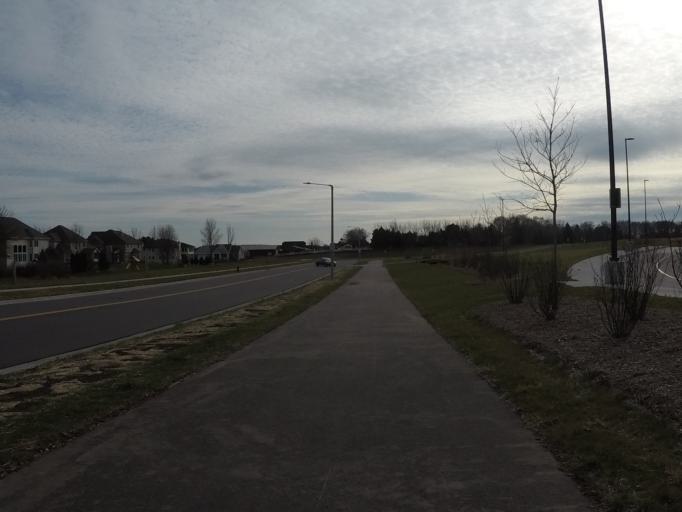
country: US
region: Wisconsin
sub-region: Dane County
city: Middleton
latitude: 43.0792
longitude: -89.5621
